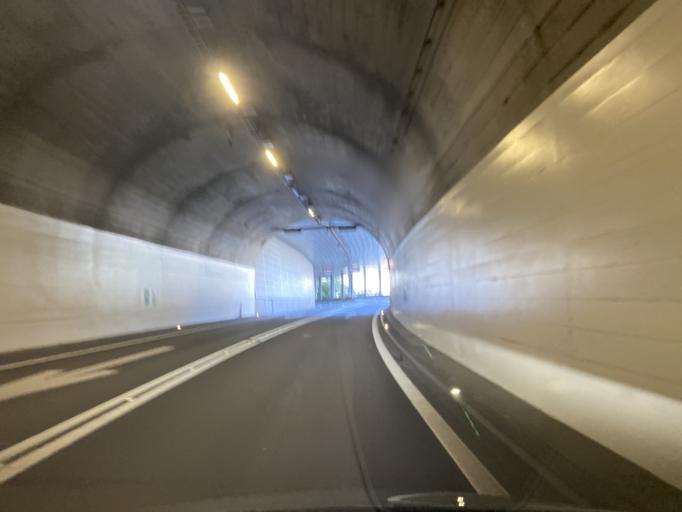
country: CH
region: Uri
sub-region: Uri
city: Flueelen
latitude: 46.9323
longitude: 8.6143
